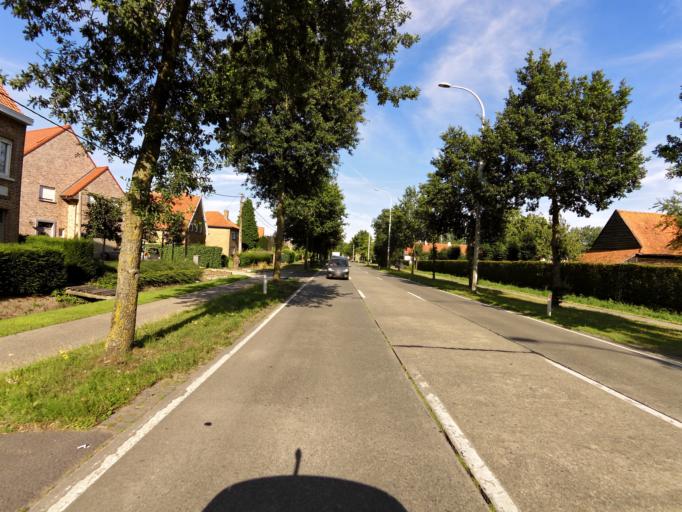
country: BE
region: Flanders
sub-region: Provincie West-Vlaanderen
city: Beernem
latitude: 51.2025
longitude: 3.3414
